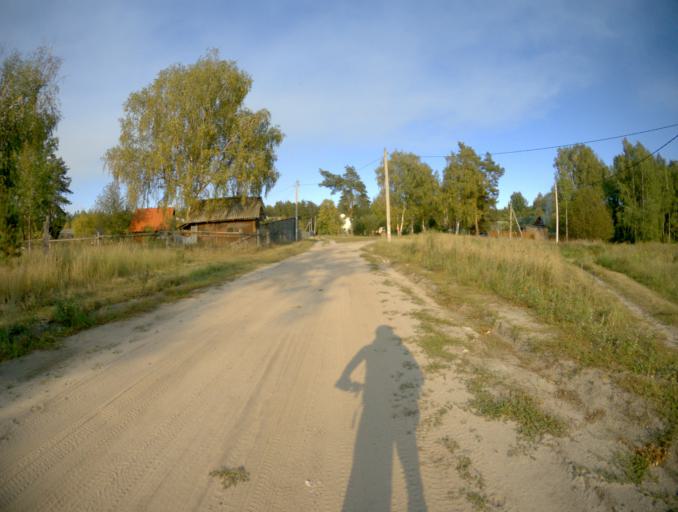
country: RU
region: Vladimir
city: Kosterevo
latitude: 55.9186
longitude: 39.7364
